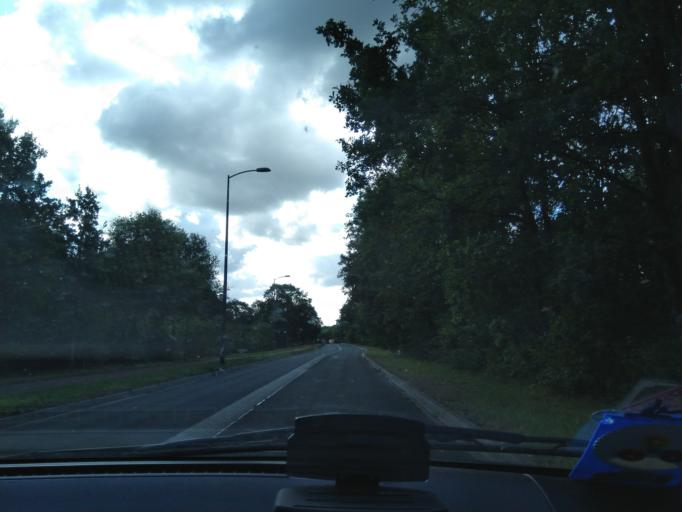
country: NL
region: North Brabant
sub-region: Gemeente Oosterhout
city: Oosterhout
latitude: 51.6191
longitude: 4.8545
